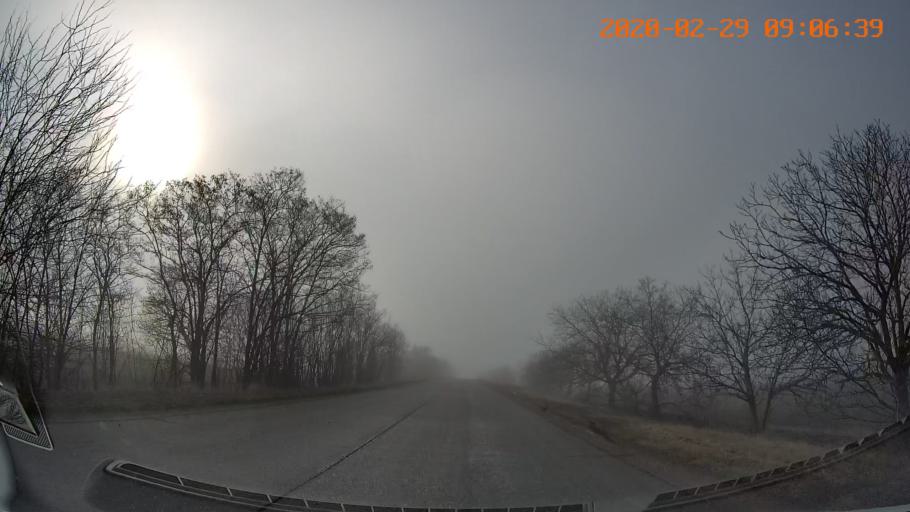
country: MD
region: Telenesti
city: Tiraspolul Nou
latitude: 46.8727
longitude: 29.7455
